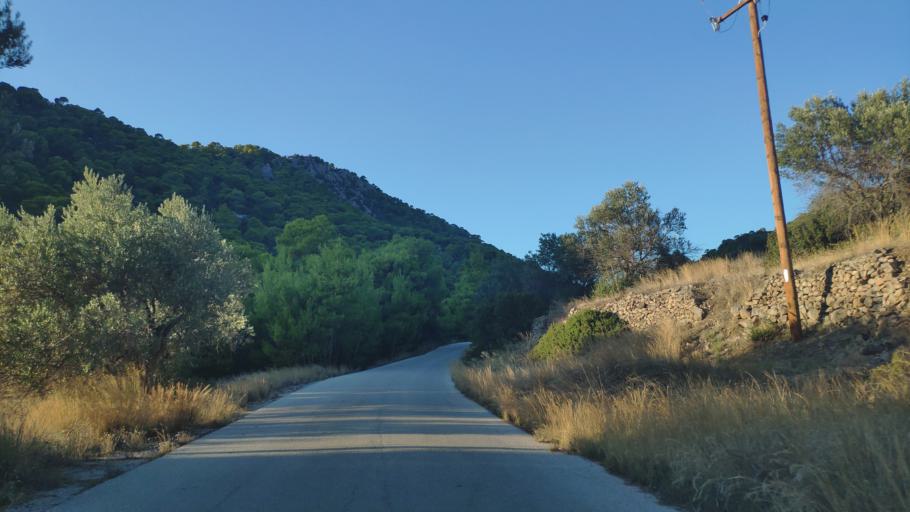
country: GR
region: Attica
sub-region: Nomos Piraios
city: Megalochori
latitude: 37.6110
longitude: 23.3280
